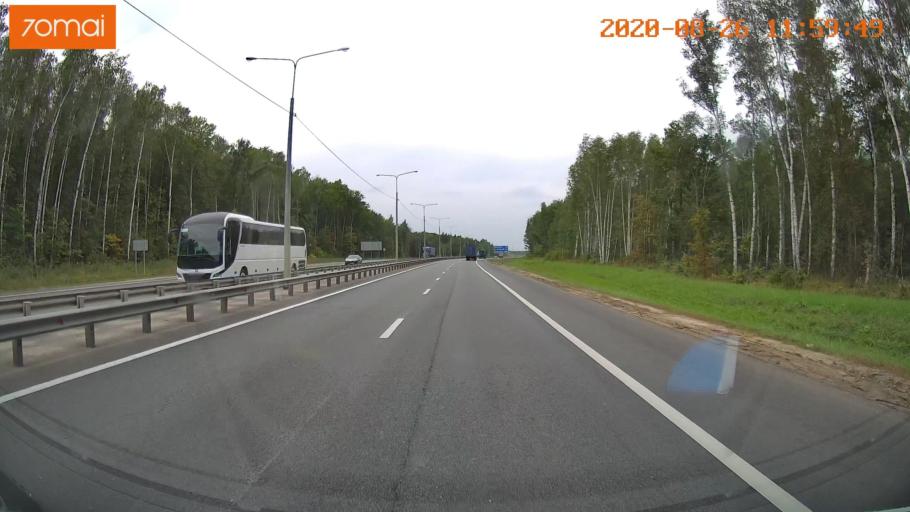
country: RU
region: Rjazan
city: Kiritsy
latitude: 54.2861
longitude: 40.2895
